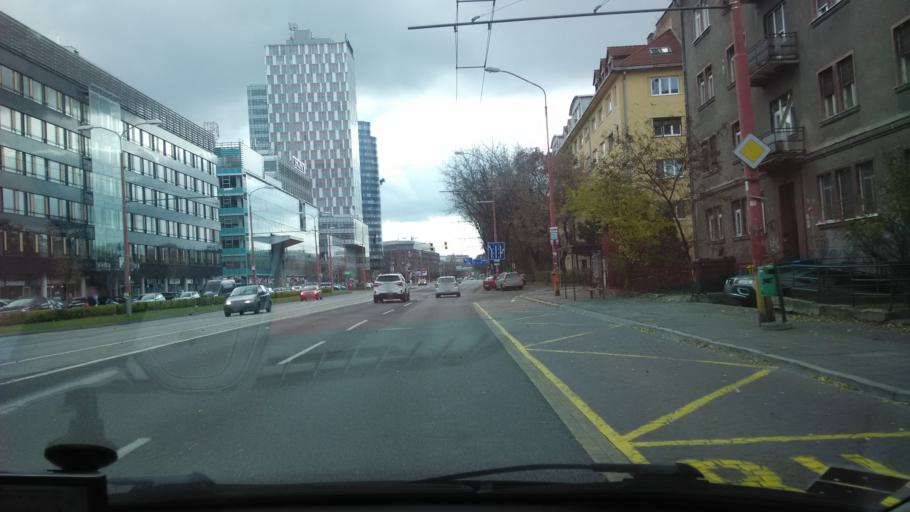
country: SK
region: Bratislavsky
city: Bratislava
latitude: 48.1506
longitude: 17.1253
